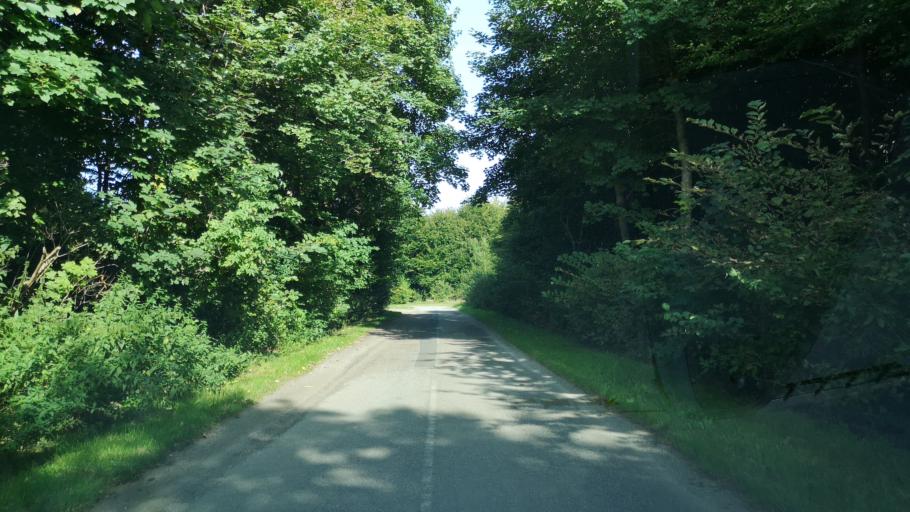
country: DK
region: Central Jutland
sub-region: Herning Kommune
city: Herning
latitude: 56.1767
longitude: 8.9528
